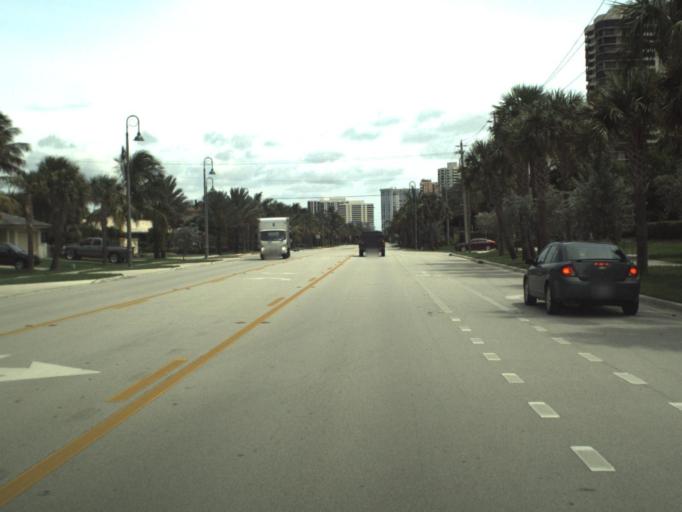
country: US
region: Florida
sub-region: Palm Beach County
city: Palm Beach Shores
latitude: 26.7934
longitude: -80.0345
